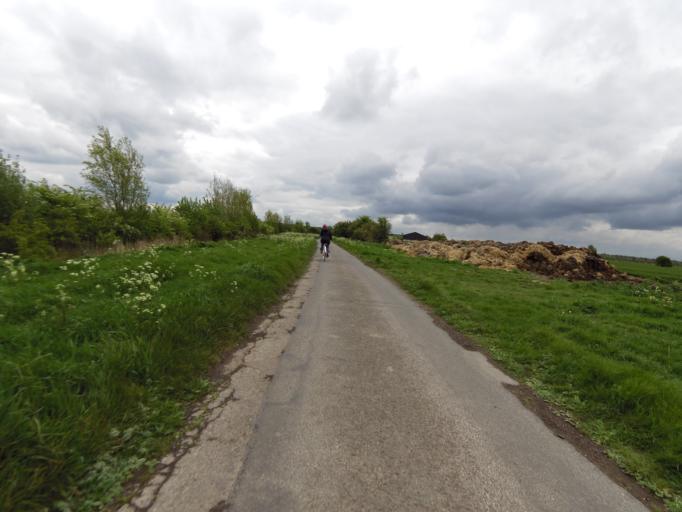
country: GB
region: England
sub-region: Cambridgeshire
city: Bottisham
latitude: 52.2711
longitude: 0.2777
